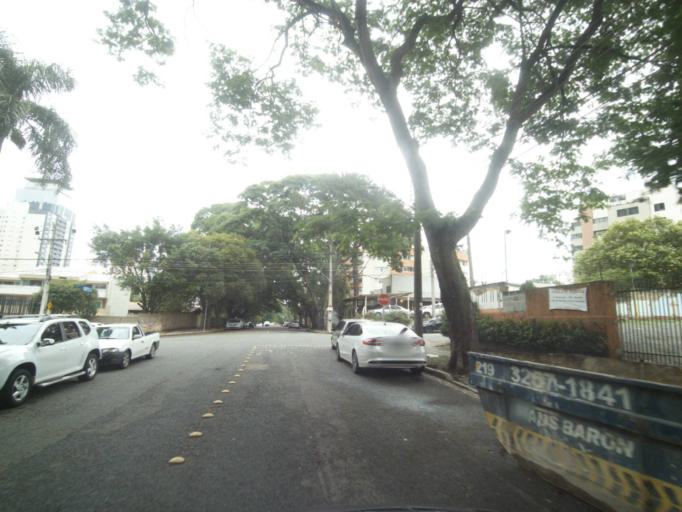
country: BR
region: Parana
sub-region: Curitiba
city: Curitiba
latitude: -25.4145
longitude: -49.2624
